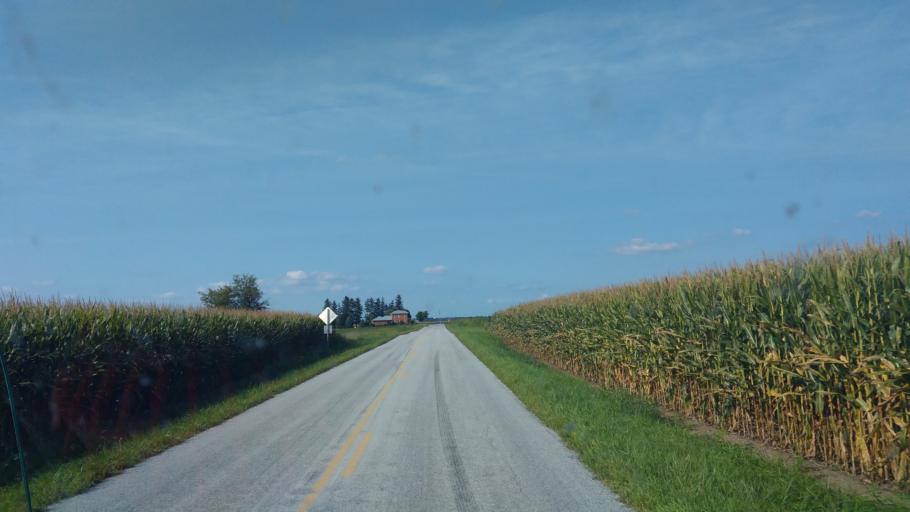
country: US
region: Ohio
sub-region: Hardin County
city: Kenton
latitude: 40.6952
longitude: -83.5934
